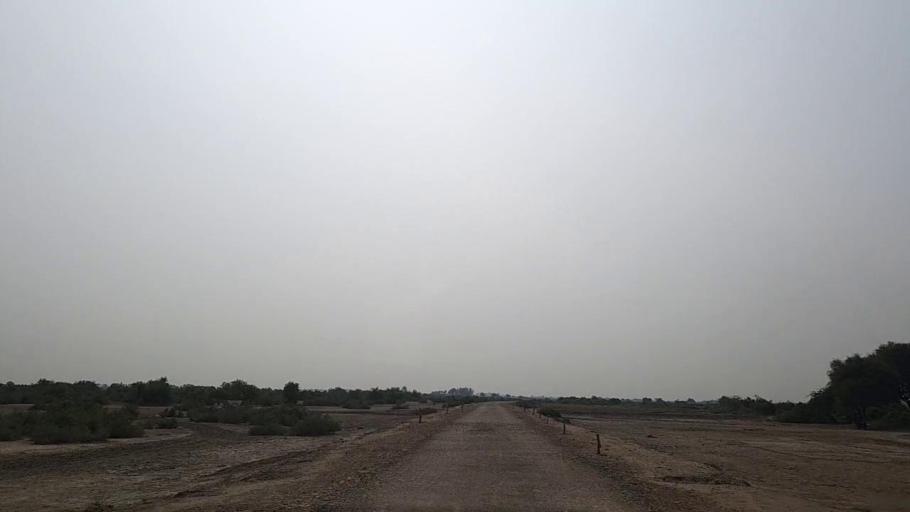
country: PK
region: Sindh
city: Mirpur Sakro
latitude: 24.6443
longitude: 67.7676
